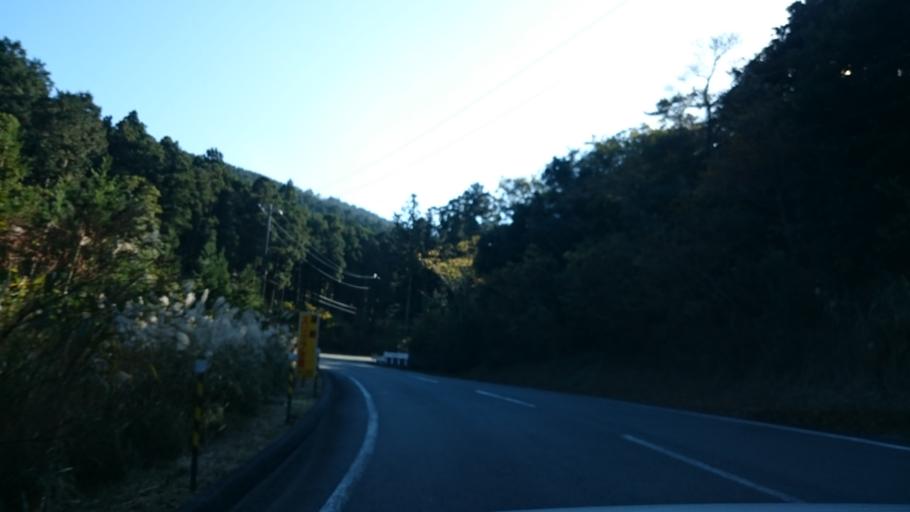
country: JP
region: Shizuoka
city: Heda
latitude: 34.9899
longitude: 138.8111
